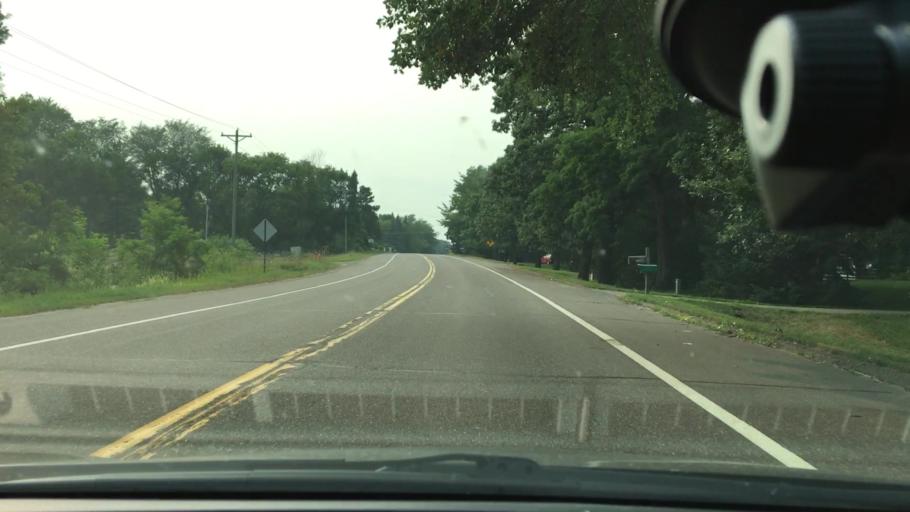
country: US
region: Minnesota
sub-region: Hennepin County
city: Champlin
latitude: 45.2086
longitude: -93.4459
